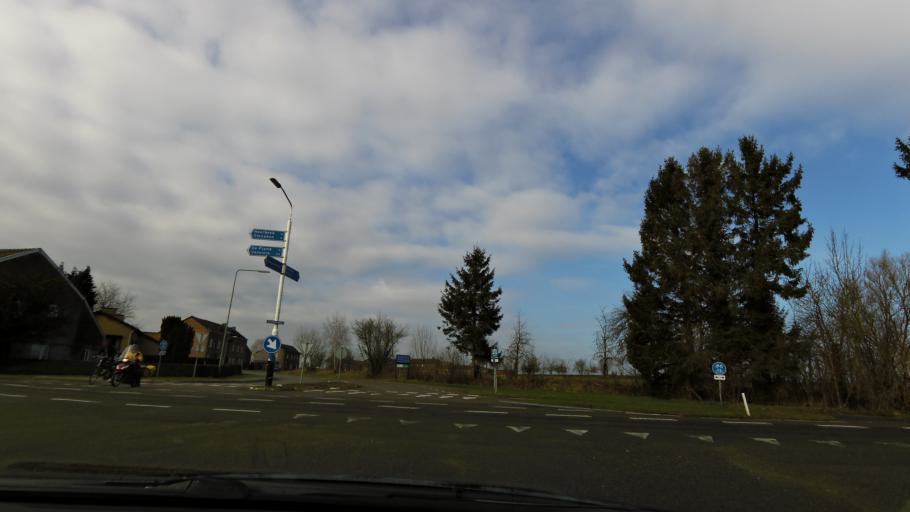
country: NL
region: Limburg
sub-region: Eijsden-Margraten
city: Margraten
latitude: 50.7953
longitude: 5.8327
